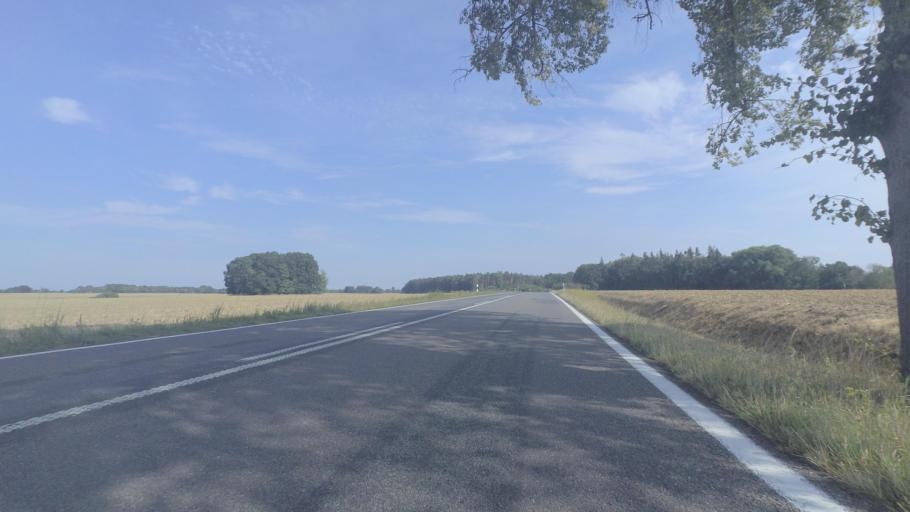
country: DE
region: Mecklenburg-Vorpommern
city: Grimmen
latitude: 54.0800
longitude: 13.1057
